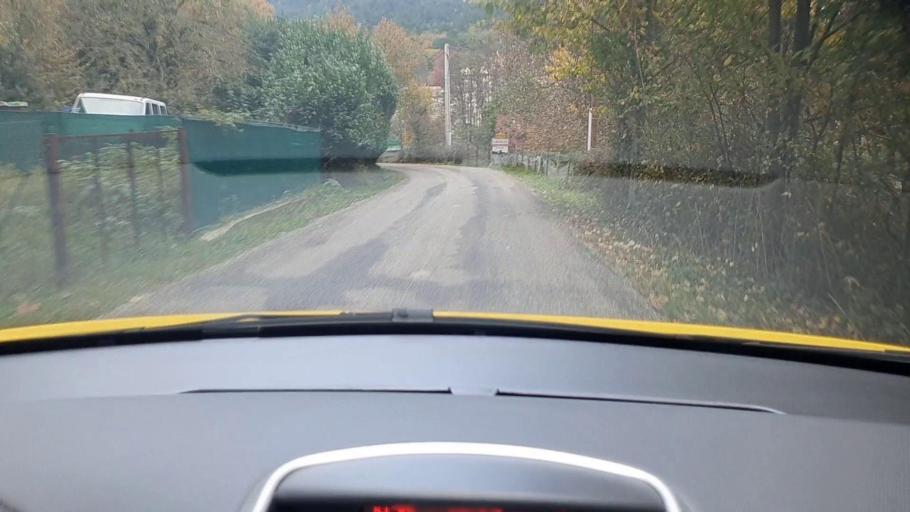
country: FR
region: Languedoc-Roussillon
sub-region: Departement du Gard
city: Lasalle
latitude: 44.0457
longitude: 3.8487
